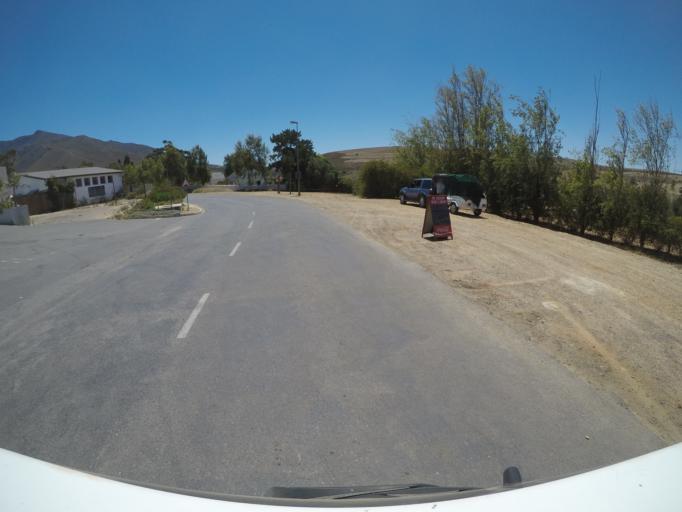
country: ZA
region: Western Cape
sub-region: Overberg District Municipality
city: Hermanus
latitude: -34.2267
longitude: 19.2075
